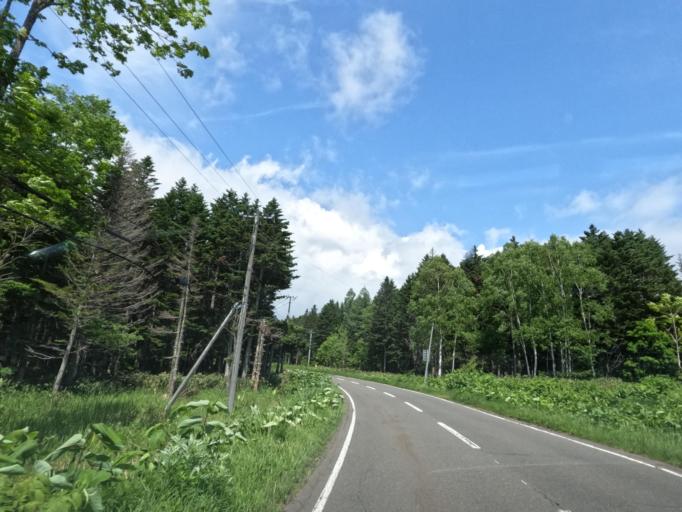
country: JP
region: Hokkaido
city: Tobetsu
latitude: 43.4114
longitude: 141.5868
